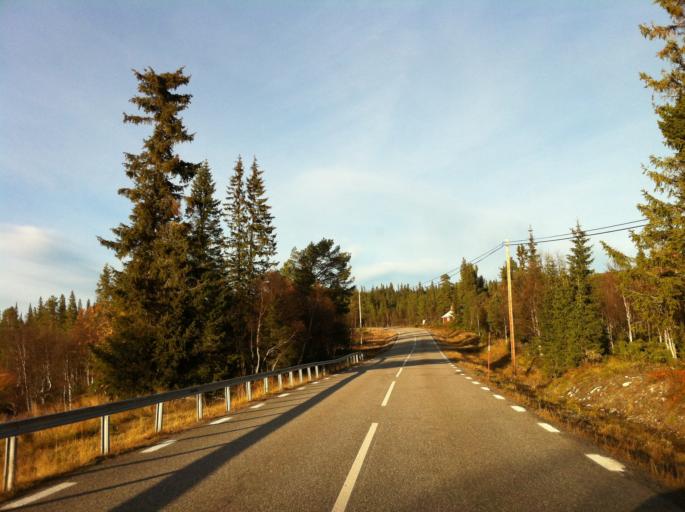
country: NO
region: Hedmark
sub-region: Engerdal
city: Engerdal
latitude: 62.0771
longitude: 12.3108
